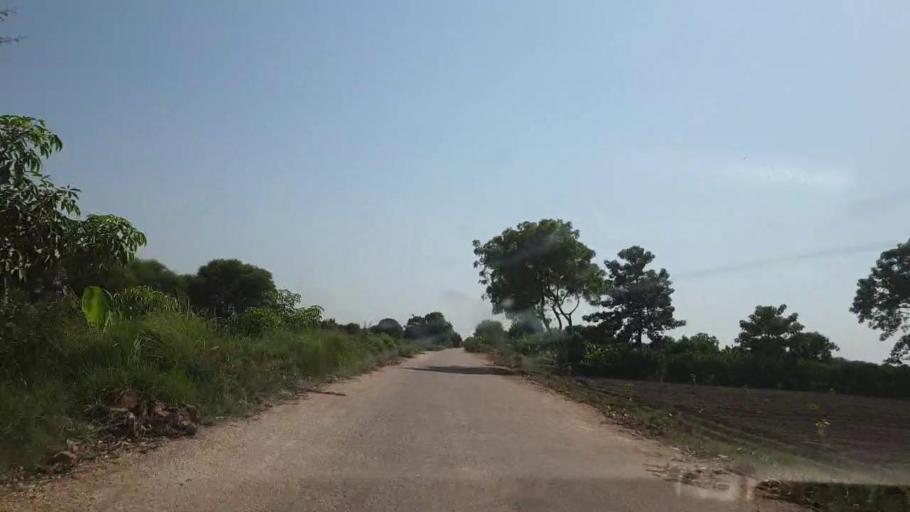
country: PK
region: Sindh
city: Tando Jam
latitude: 25.4173
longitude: 68.5821
